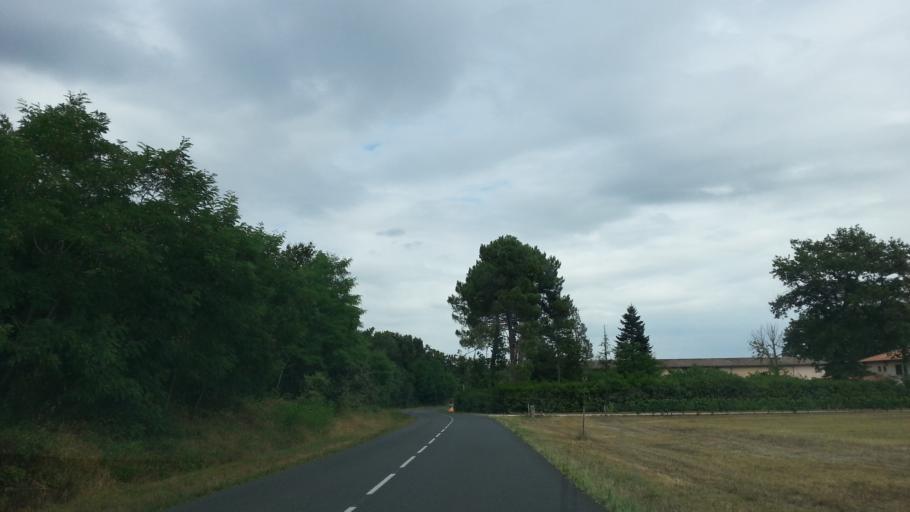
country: FR
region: Aquitaine
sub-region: Departement de la Gironde
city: Illats
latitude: 44.5852
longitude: -0.3960
